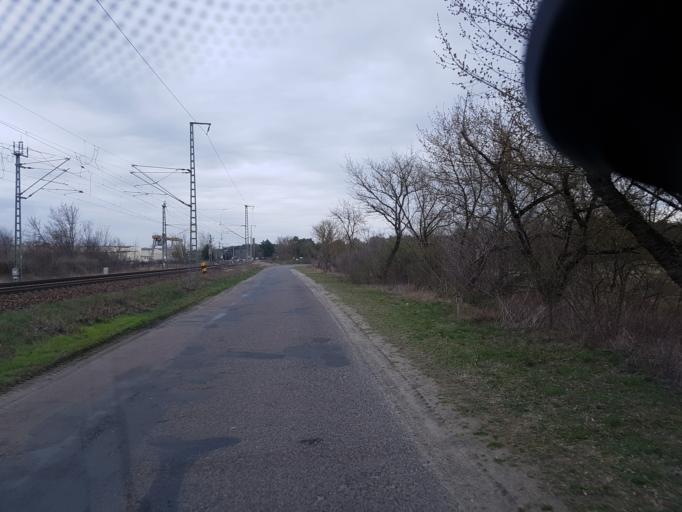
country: DE
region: Brandenburg
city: Eisenhuettenstadt
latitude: 52.1521
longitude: 14.6592
